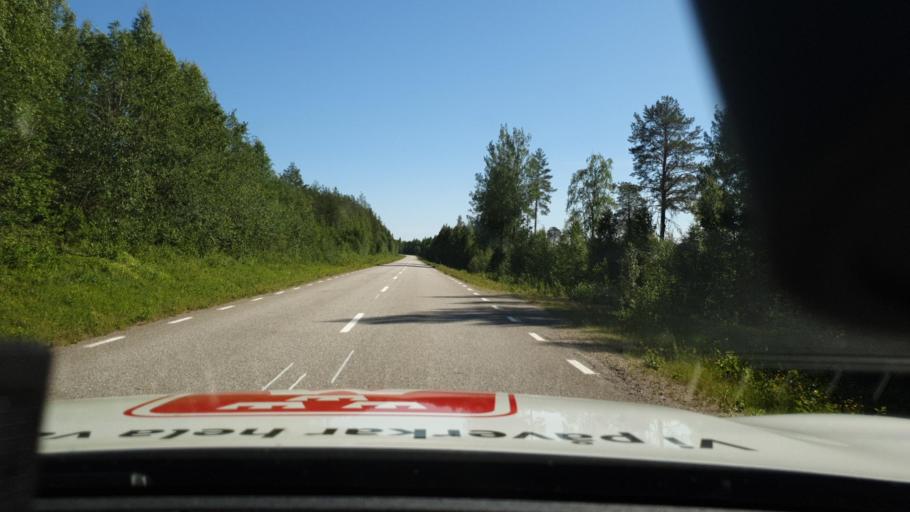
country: SE
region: Norrbotten
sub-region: Lulea Kommun
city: Ranea
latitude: 66.0208
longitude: 22.2990
